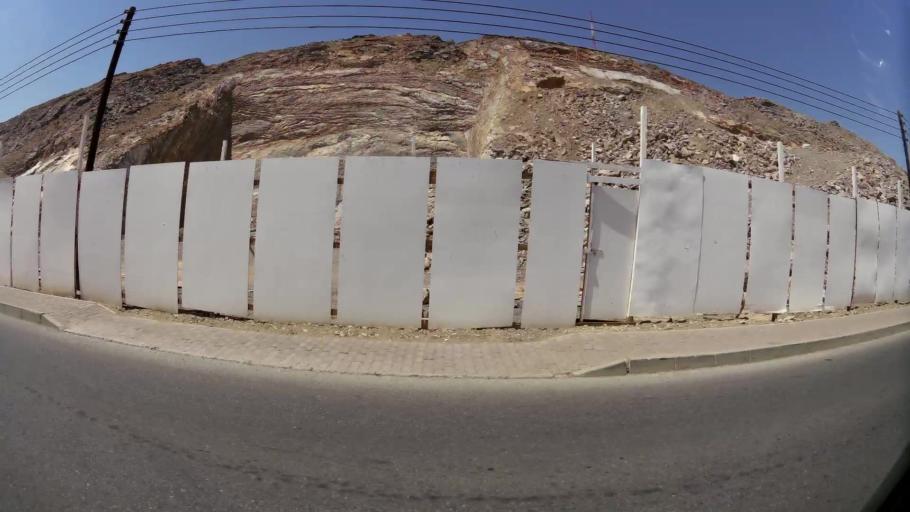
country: OM
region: Muhafazat Masqat
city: Muscat
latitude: 23.5957
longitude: 58.5392
